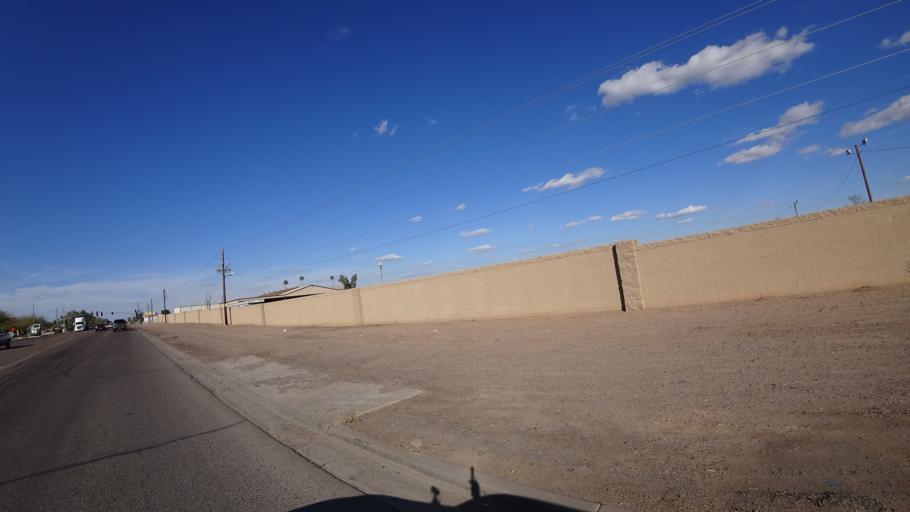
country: US
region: Arizona
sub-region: Maricopa County
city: Tolleson
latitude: 33.4390
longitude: -112.2383
